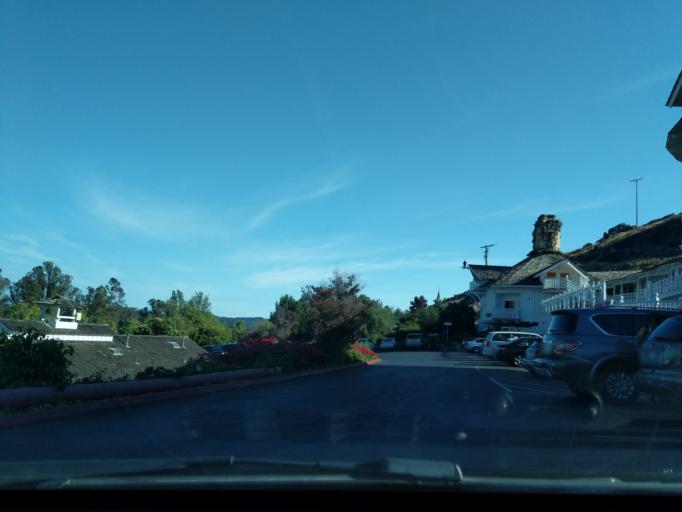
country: US
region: California
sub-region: San Luis Obispo County
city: San Luis Obispo
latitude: 35.2684
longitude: -120.6760
